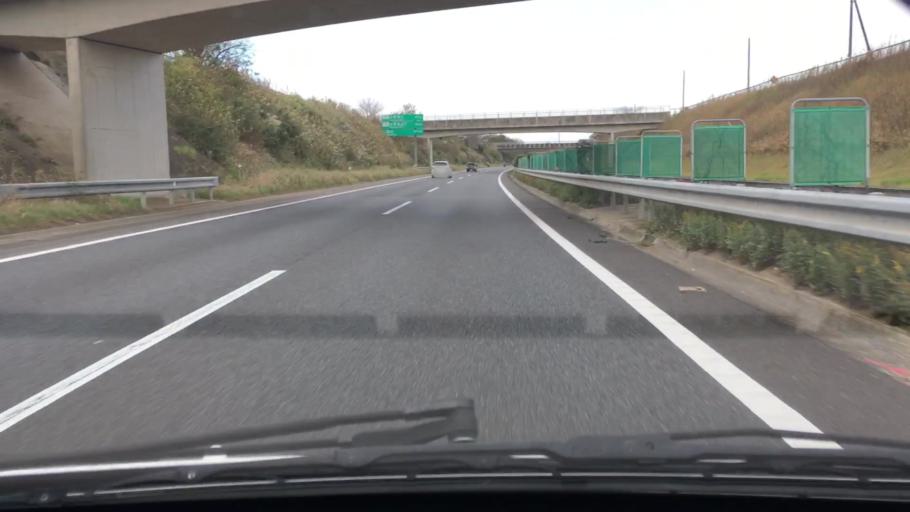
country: JP
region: Chiba
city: Ichihara
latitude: 35.4248
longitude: 140.0323
